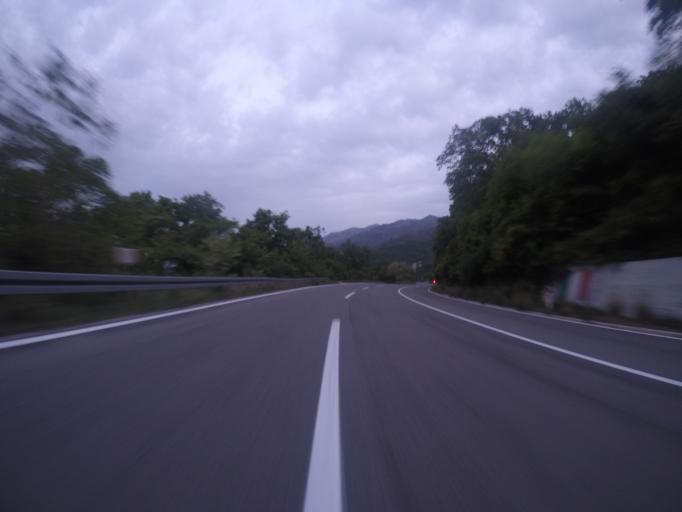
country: ME
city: Petrovac na Moru
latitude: 42.1916
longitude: 18.9859
